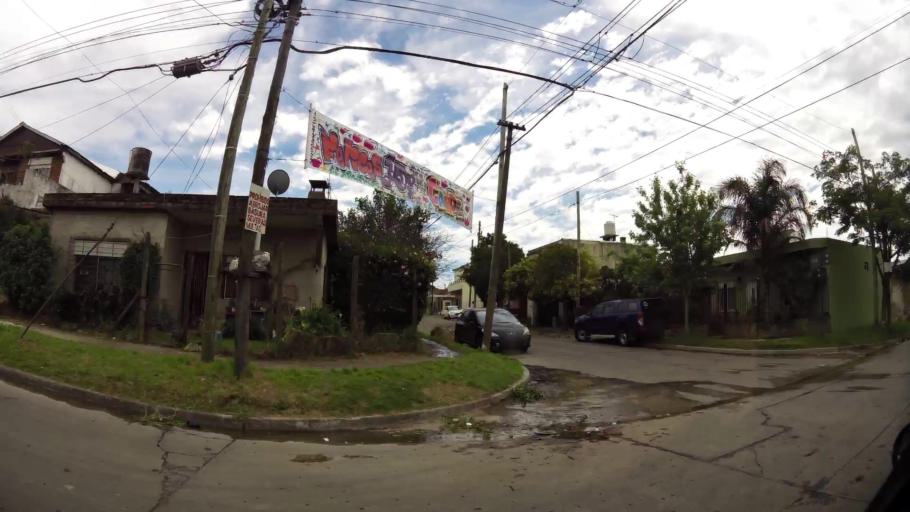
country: AR
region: Buenos Aires
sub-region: Partido de Quilmes
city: Quilmes
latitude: -34.7565
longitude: -58.2326
